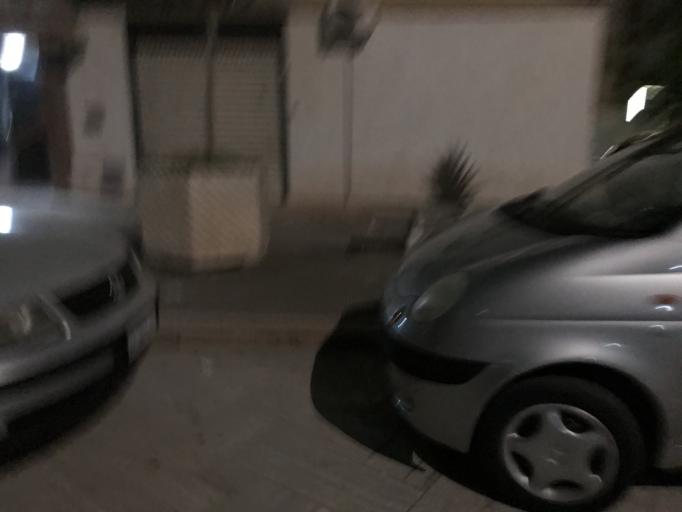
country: IT
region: Apulia
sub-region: Provincia di Bari
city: Corato
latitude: 41.1577
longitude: 16.4025
